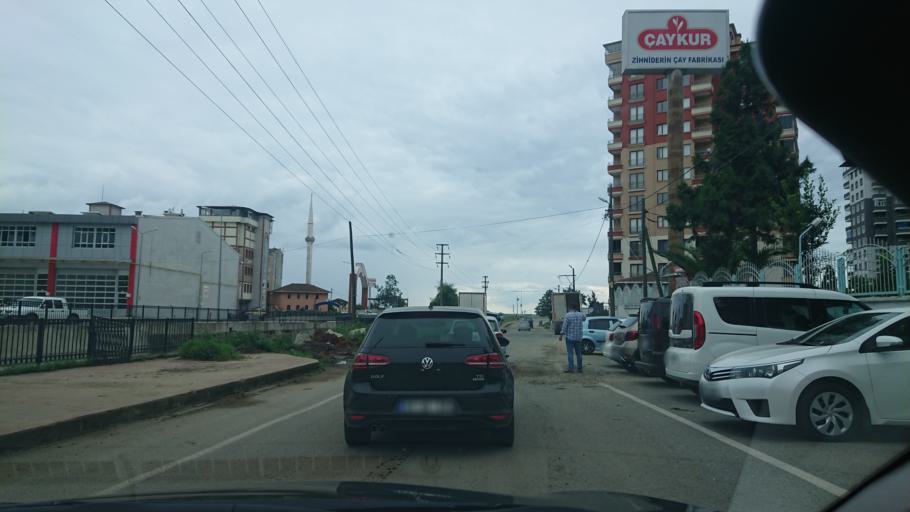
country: TR
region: Rize
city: Rize
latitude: 41.0333
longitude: 40.4814
